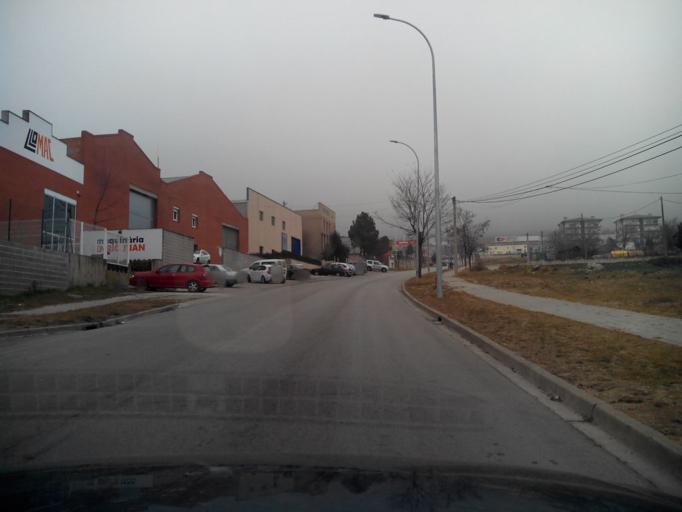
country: ES
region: Catalonia
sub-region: Provincia de Barcelona
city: Berga
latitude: 42.0914
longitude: 1.8275
